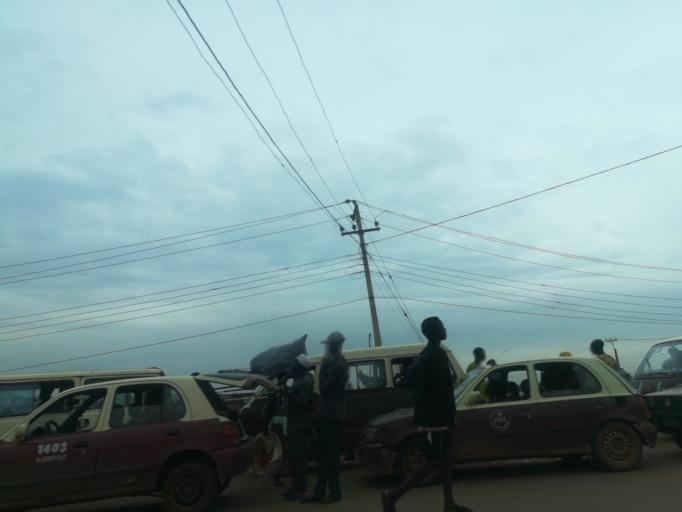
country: NG
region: Oyo
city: Ibadan
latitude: 7.3972
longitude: 3.9208
